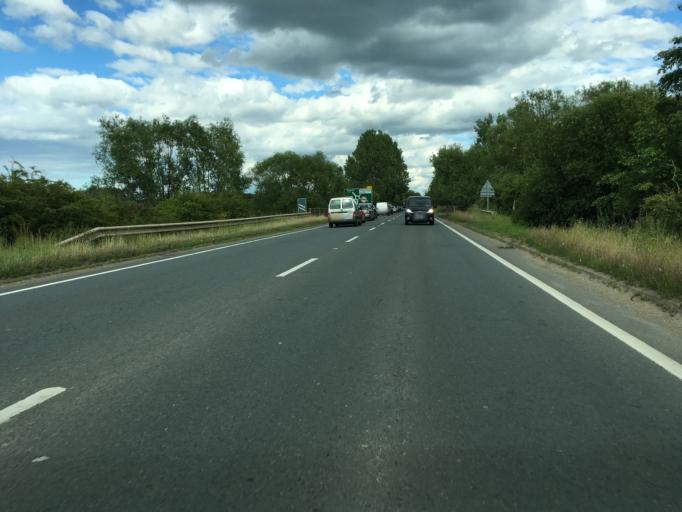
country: GB
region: England
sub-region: Oxfordshire
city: Thame
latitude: 51.7551
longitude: -0.9824
